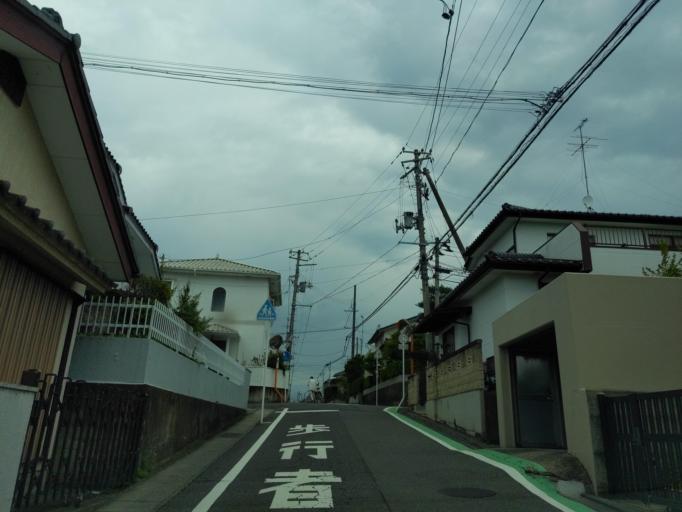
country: JP
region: Fukushima
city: Koriyama
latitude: 37.3749
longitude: 140.3454
